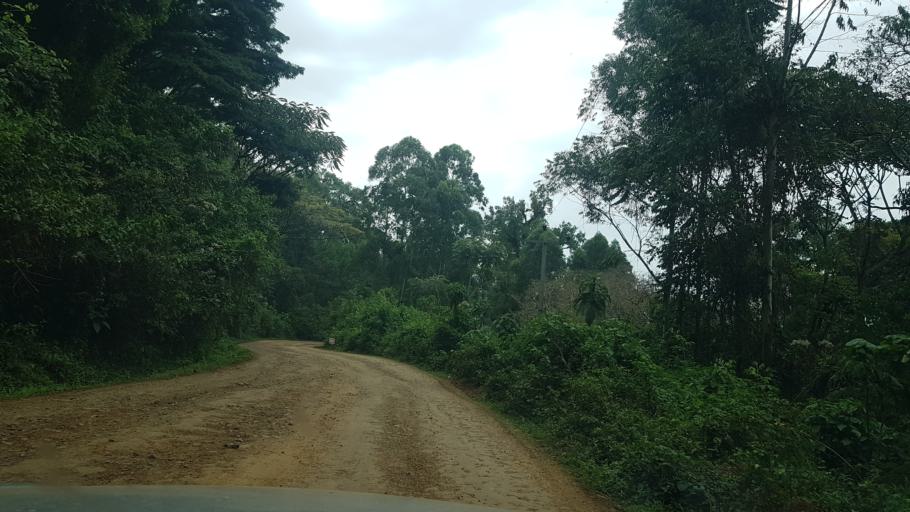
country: ET
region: Oromiya
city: Gore
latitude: 7.8195
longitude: 35.4600
